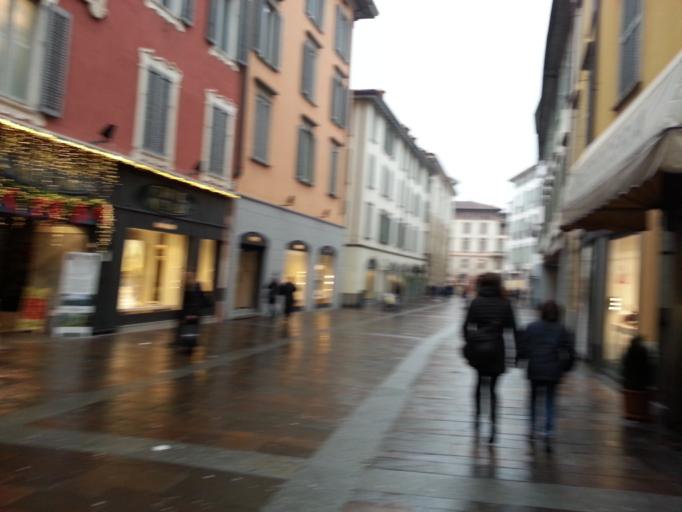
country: IT
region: Lombardy
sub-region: Provincia di Bergamo
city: Bergamo
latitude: 45.6929
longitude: 9.6654
